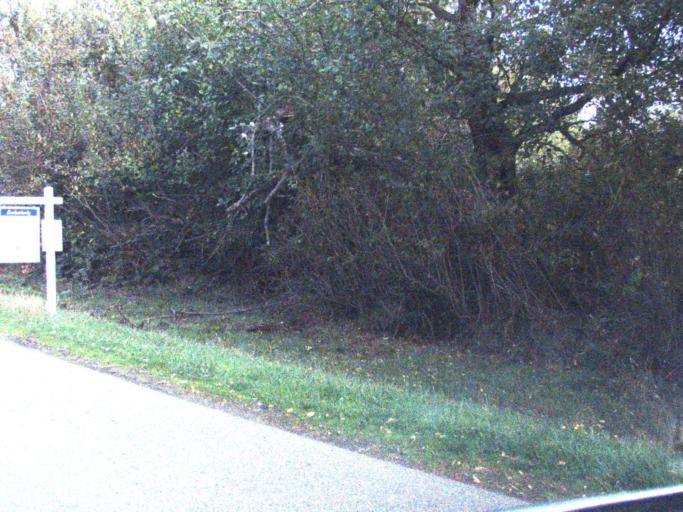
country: US
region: Washington
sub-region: Jefferson County
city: Port Hadlock-Irondale
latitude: 48.0361
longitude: -122.8237
